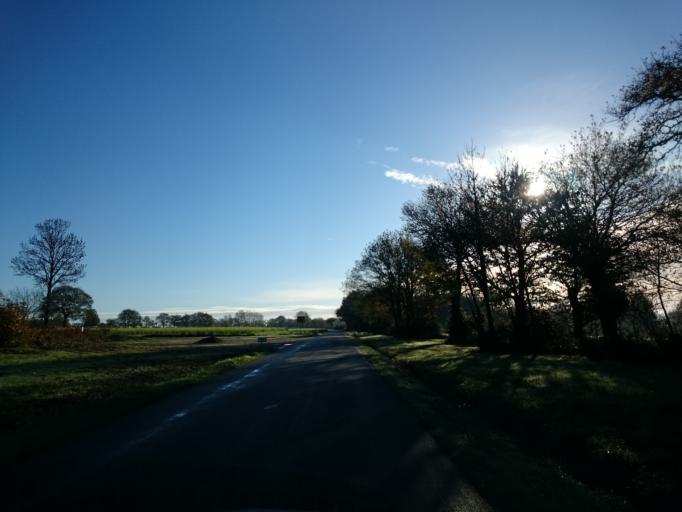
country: FR
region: Brittany
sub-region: Departement d'Ille-et-Vilaine
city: Chanteloup
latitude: 47.9258
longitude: -1.6032
